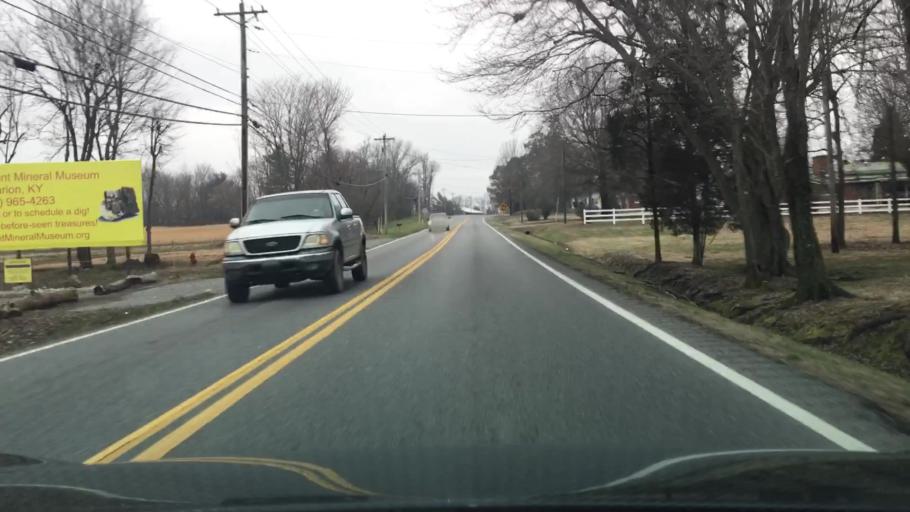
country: US
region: Kentucky
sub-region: McCracken County
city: Reidland
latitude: 36.9867
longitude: -88.5001
